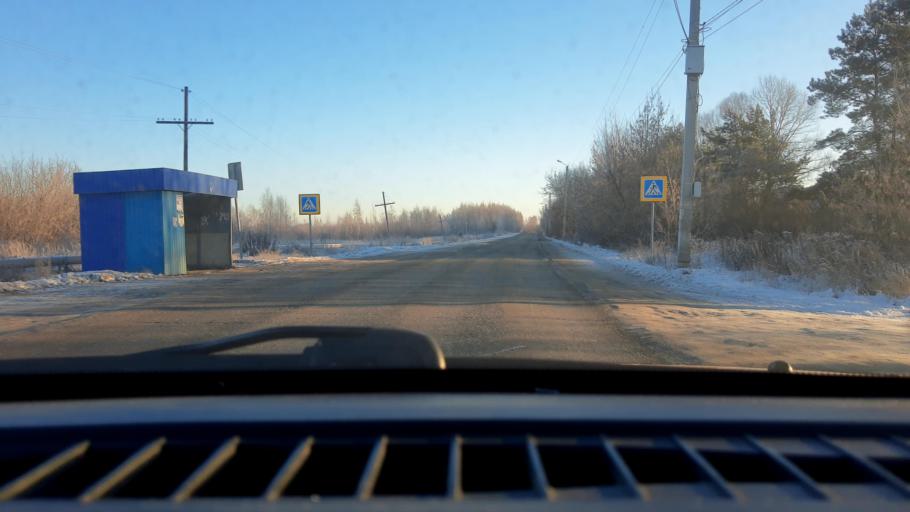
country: RU
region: Nizjnij Novgorod
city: Bor
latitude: 56.3688
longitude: 44.1070
